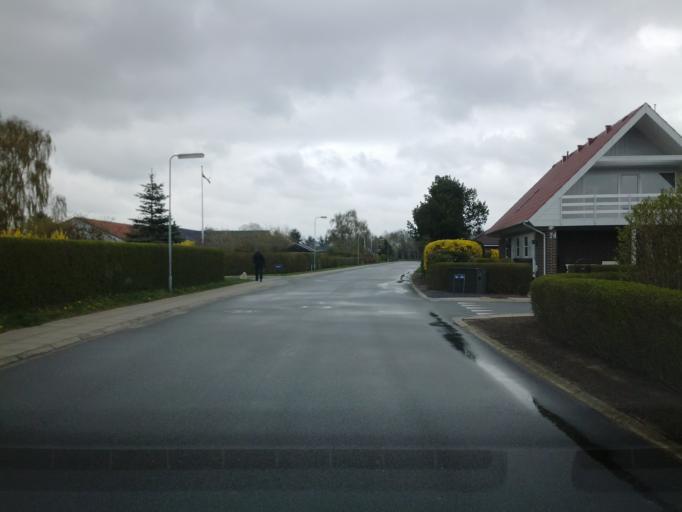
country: DK
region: North Denmark
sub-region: Bronderslev Kommune
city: Hjallerup
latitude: 57.1603
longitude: 10.1476
